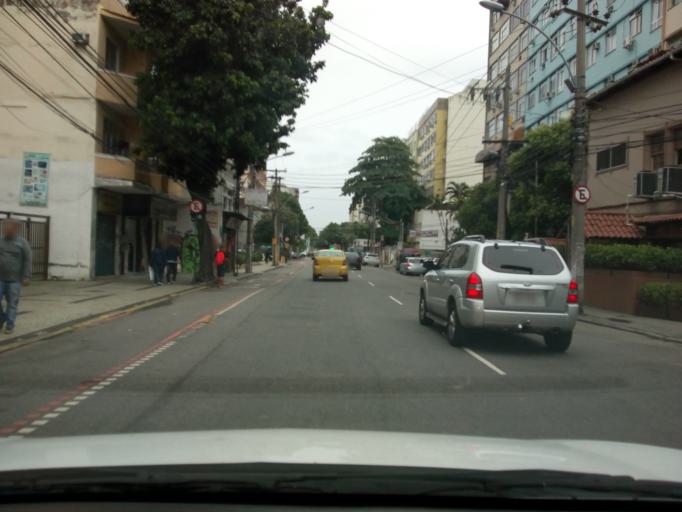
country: BR
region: Rio de Janeiro
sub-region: Rio De Janeiro
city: Rio de Janeiro
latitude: -22.9223
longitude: -43.2327
